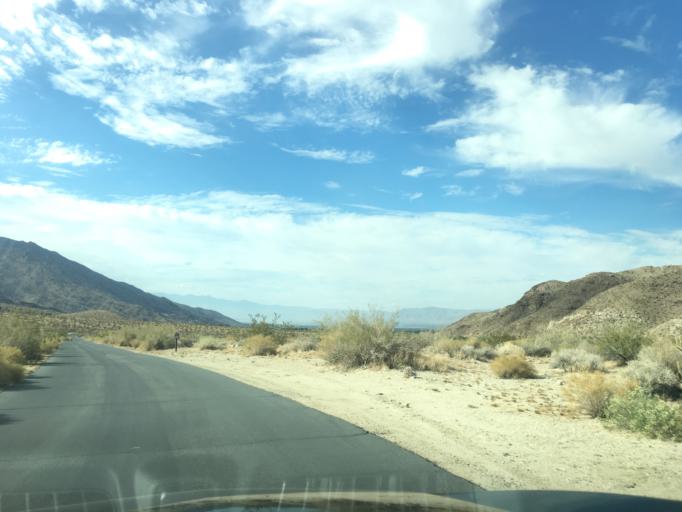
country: US
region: California
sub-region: Riverside County
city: Cathedral City
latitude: 33.7457
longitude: -116.5373
